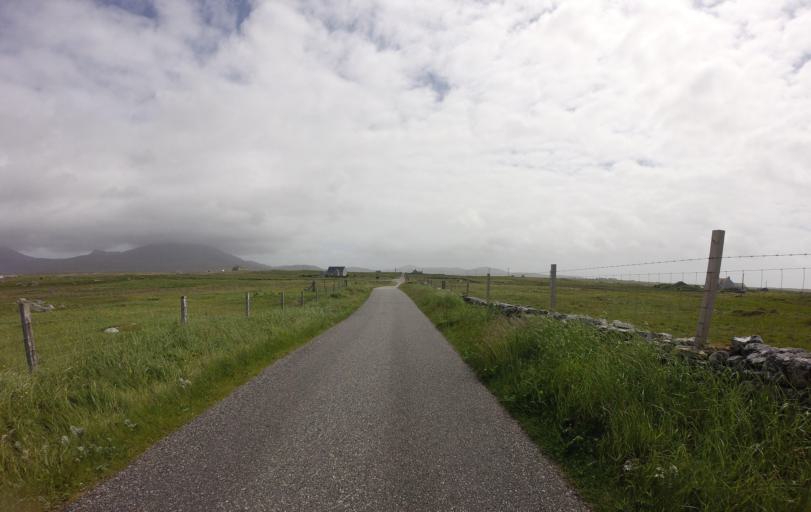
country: GB
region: Scotland
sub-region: Eilean Siar
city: Isle of South Uist
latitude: 57.2780
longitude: -7.4131
